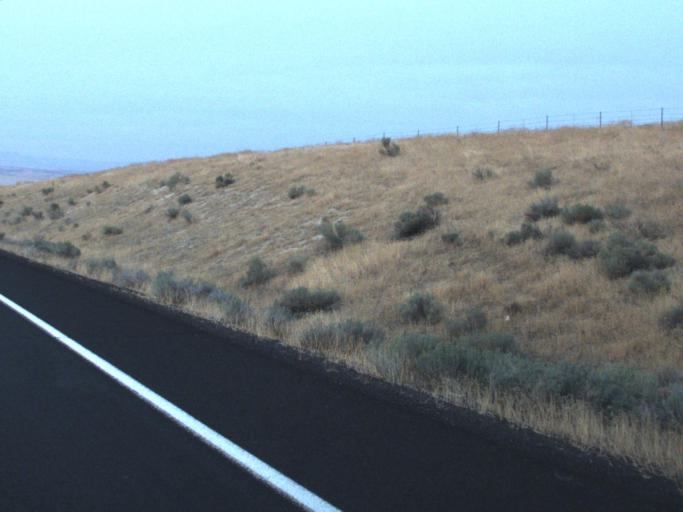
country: US
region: Washington
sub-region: Yakima County
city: Toppenish
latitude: 46.2735
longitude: -120.4002
